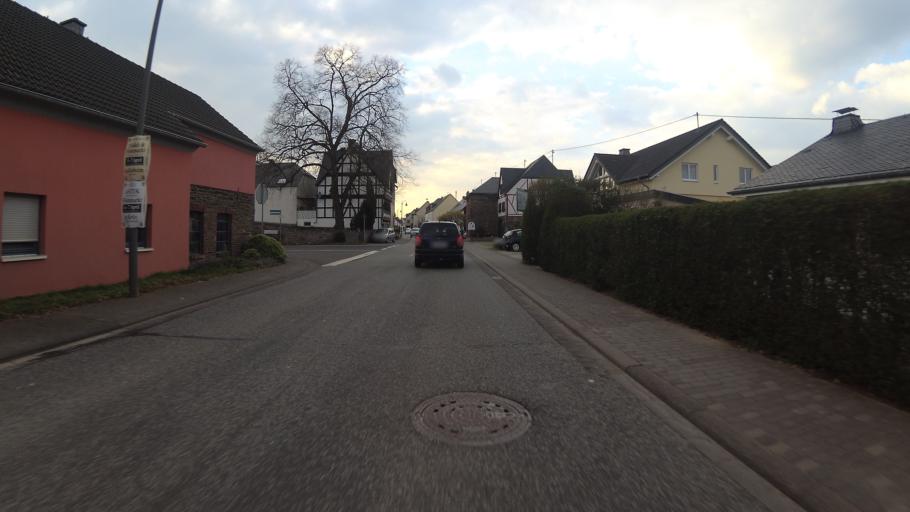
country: DE
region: Rheinland-Pfalz
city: Monzelfeld
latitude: 49.9086
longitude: 7.0446
